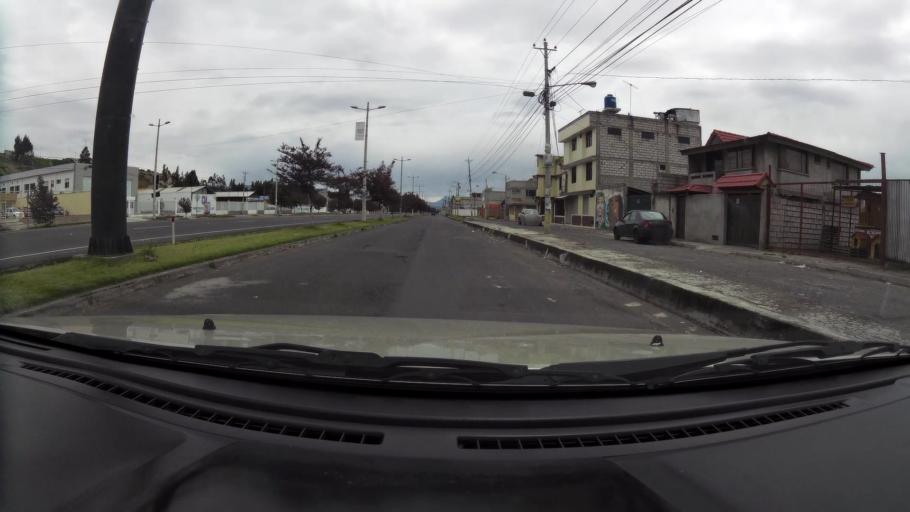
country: EC
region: Cotopaxi
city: Latacunga
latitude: -0.9623
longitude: -78.6114
